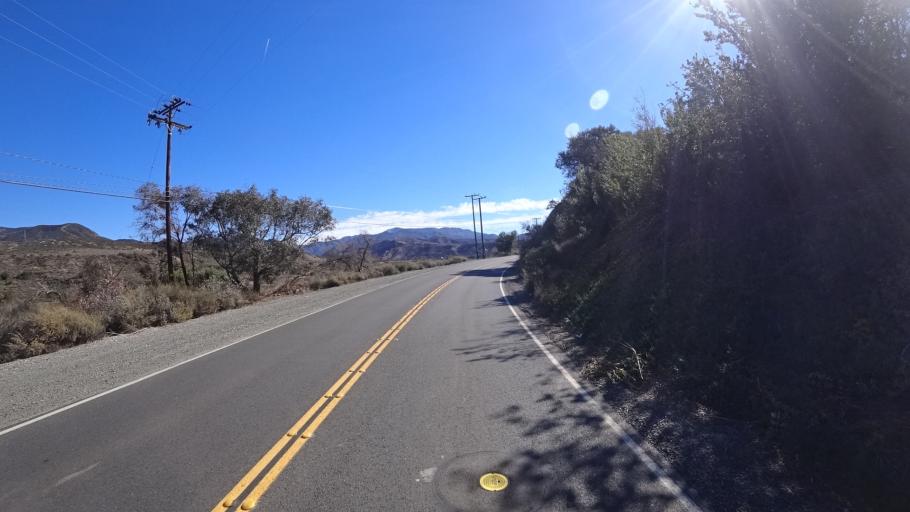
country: US
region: California
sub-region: Orange County
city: Foothill Ranch
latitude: 33.7493
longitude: -117.6700
